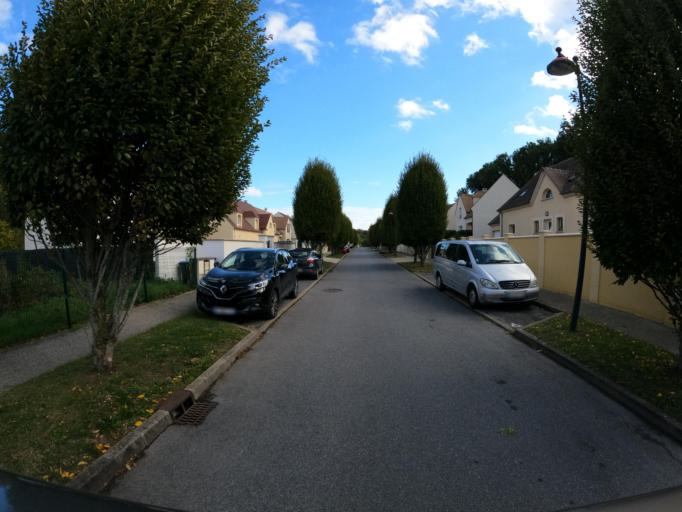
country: FR
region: Ile-de-France
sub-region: Departement de Seine-et-Marne
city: Esbly
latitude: 48.8935
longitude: 2.8146
